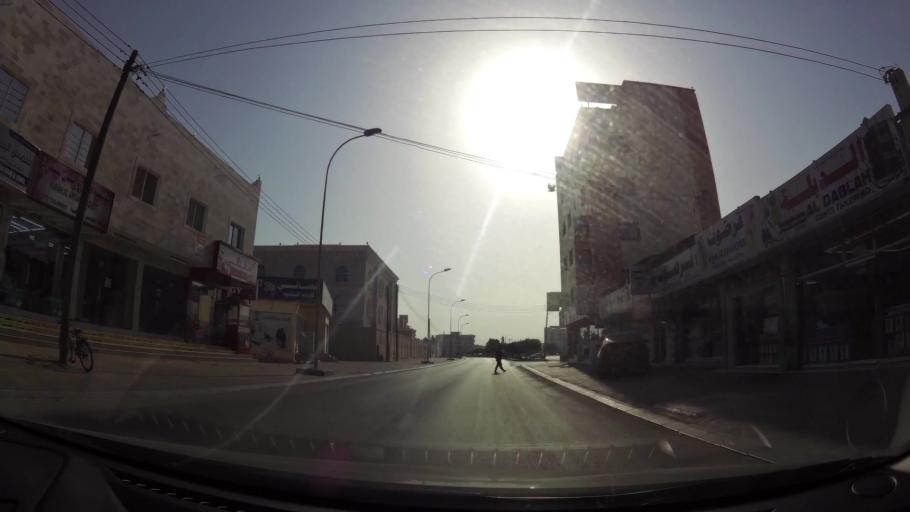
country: OM
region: Zufar
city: Salalah
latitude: 17.0093
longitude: 54.0978
